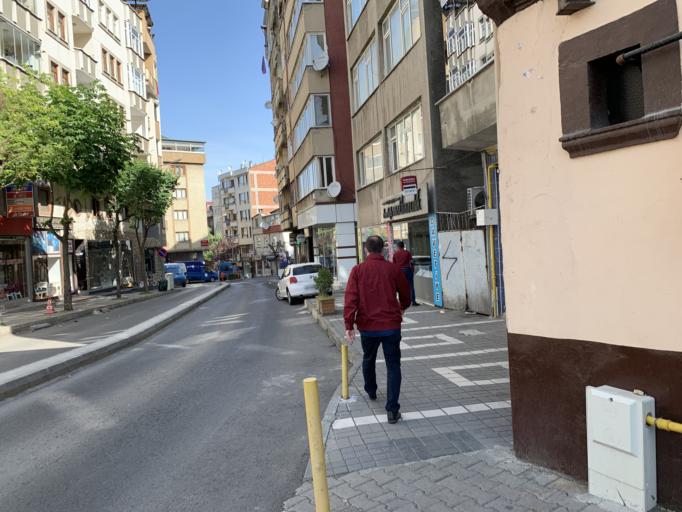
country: TR
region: Trabzon
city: Trabzon
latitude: 41.0041
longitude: 39.7239
